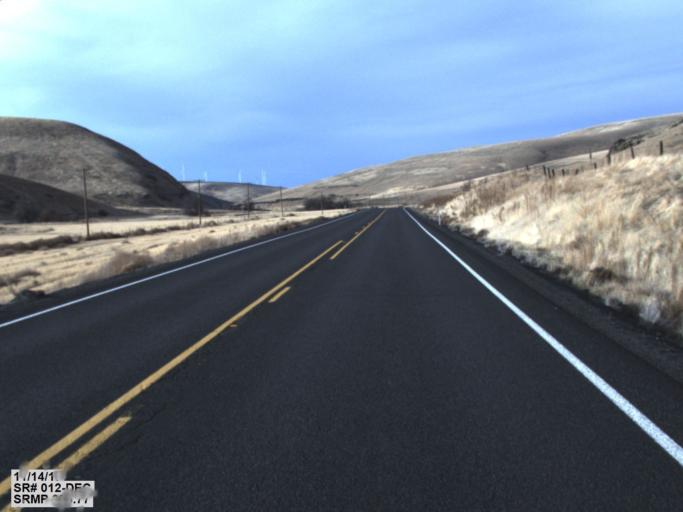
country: US
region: Washington
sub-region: Garfield County
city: Pomeroy
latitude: 46.4754
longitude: -117.7277
